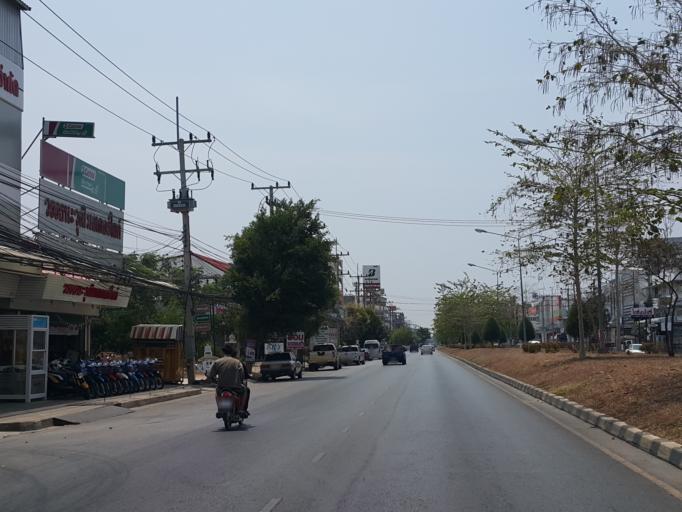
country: TH
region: Kanchanaburi
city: Kanchanaburi
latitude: 14.0395
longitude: 99.5174
